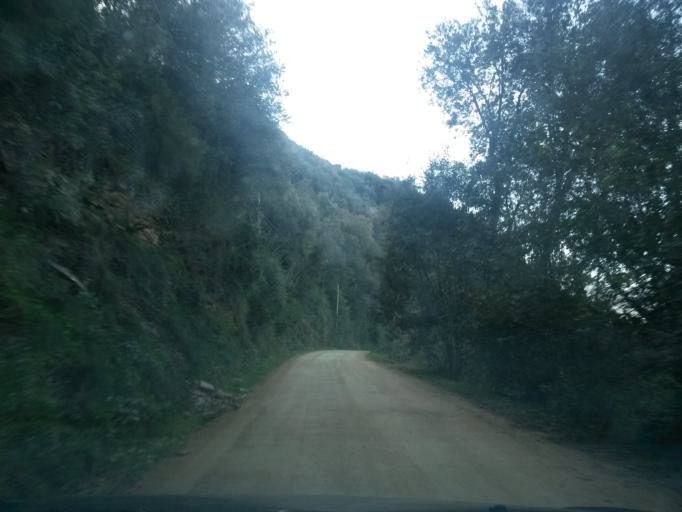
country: ES
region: Catalonia
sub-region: Provincia de Girona
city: la Cellera de Ter
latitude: 41.9779
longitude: 2.6302
